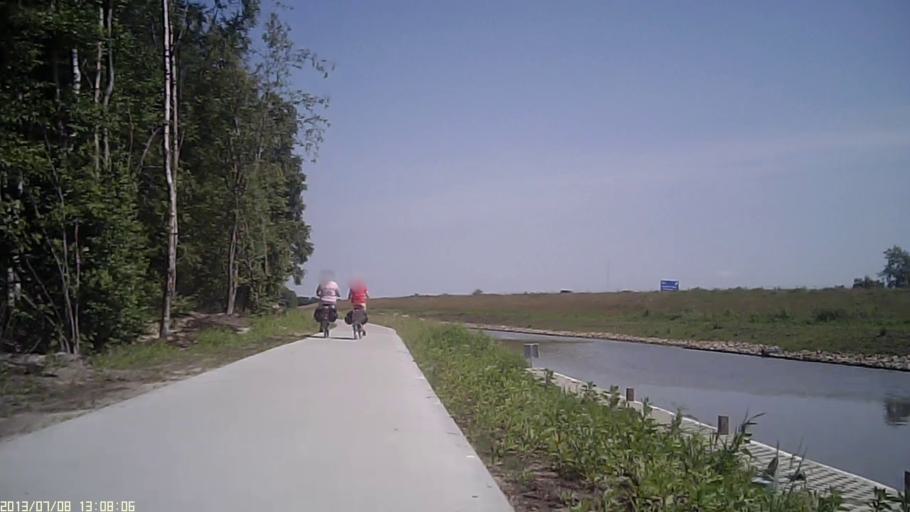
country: NL
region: Drenthe
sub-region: Gemeente Emmen
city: Klazienaveen
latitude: 52.7346
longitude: 6.9602
